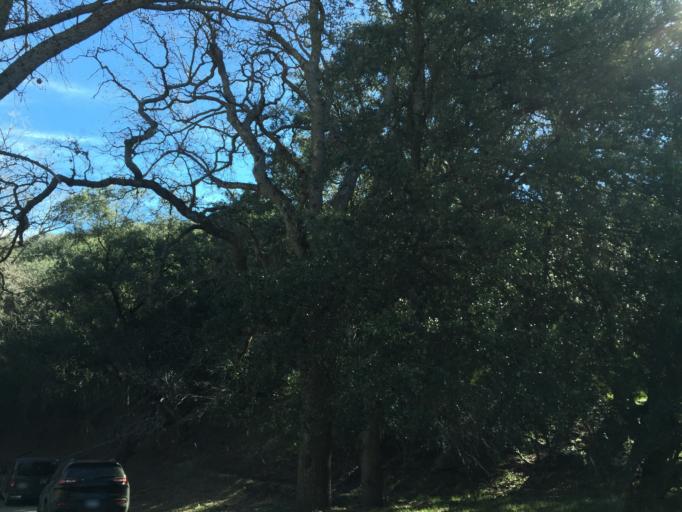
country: US
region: California
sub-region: Kern County
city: Lebec
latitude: 34.8914
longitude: -118.7468
